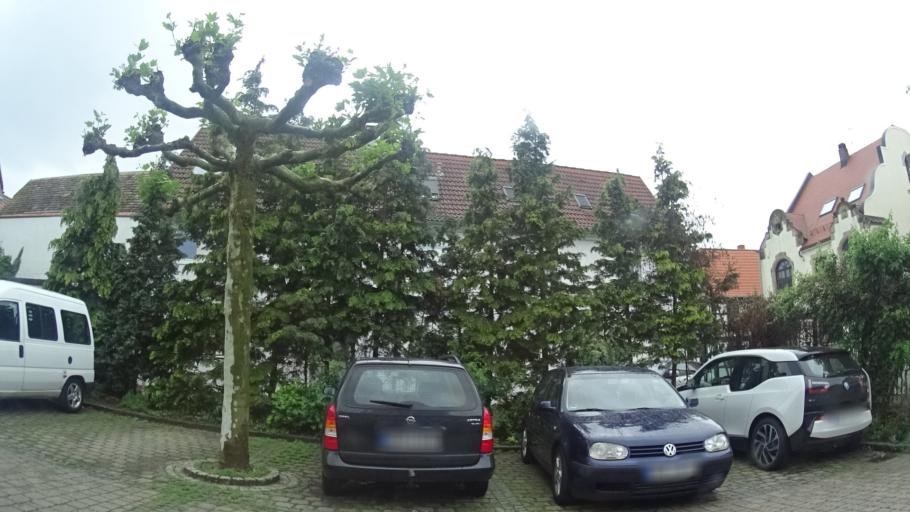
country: DE
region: Rheinland-Pfalz
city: Bellheim
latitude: 49.1912
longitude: 8.2769
